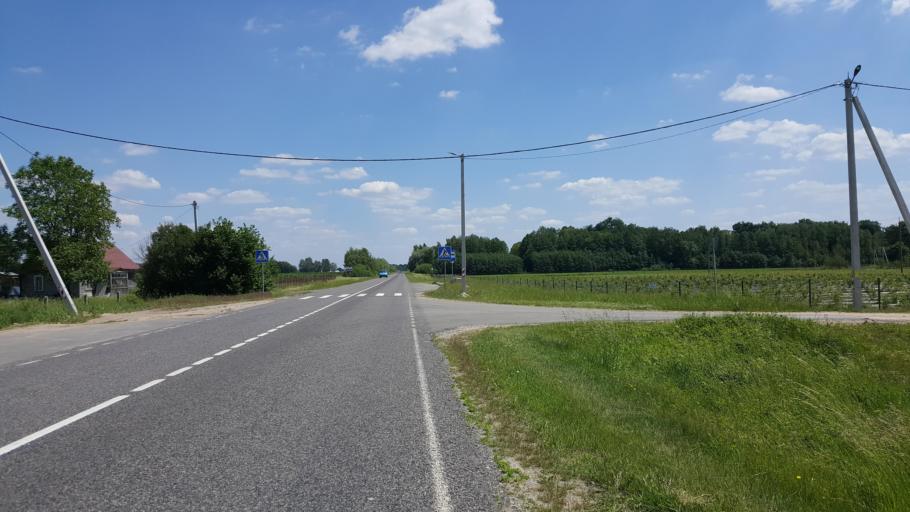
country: BY
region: Brest
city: Kobryn
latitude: 52.2016
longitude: 24.2009
